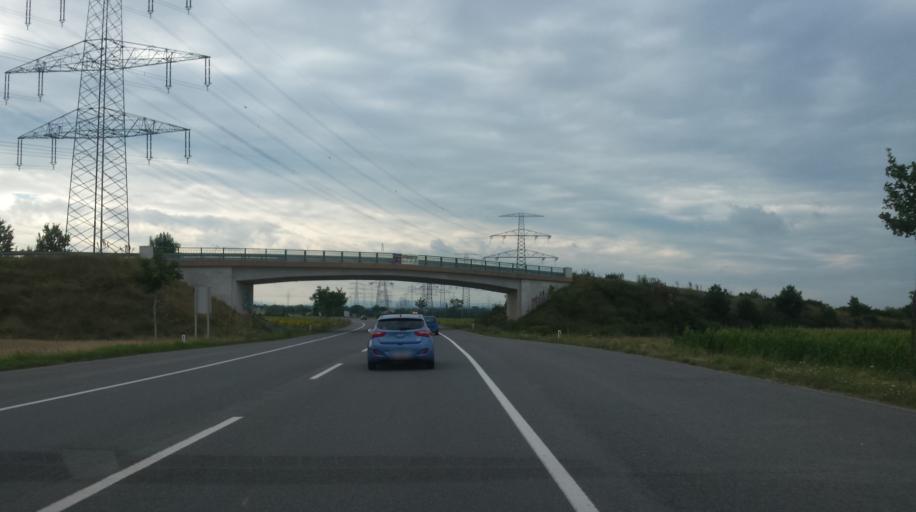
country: AT
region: Lower Austria
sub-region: Politischer Bezirk Wien-Umgebung
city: Himberg
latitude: 48.0883
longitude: 16.4541
